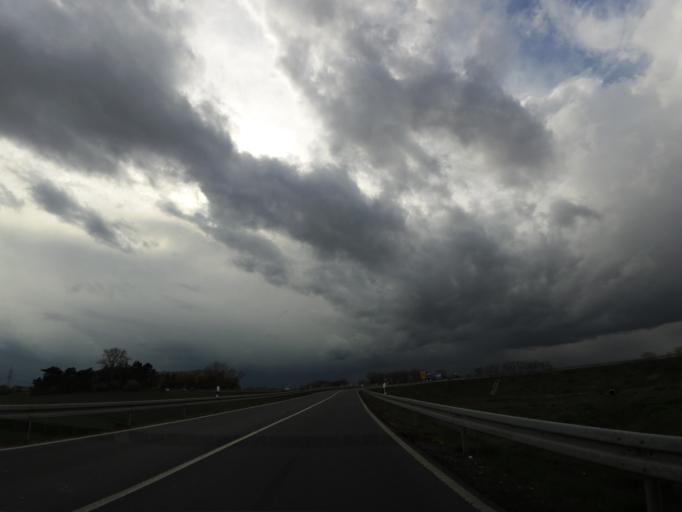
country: DE
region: Saxony-Anhalt
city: Ditfurt
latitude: 51.8044
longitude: 11.1963
